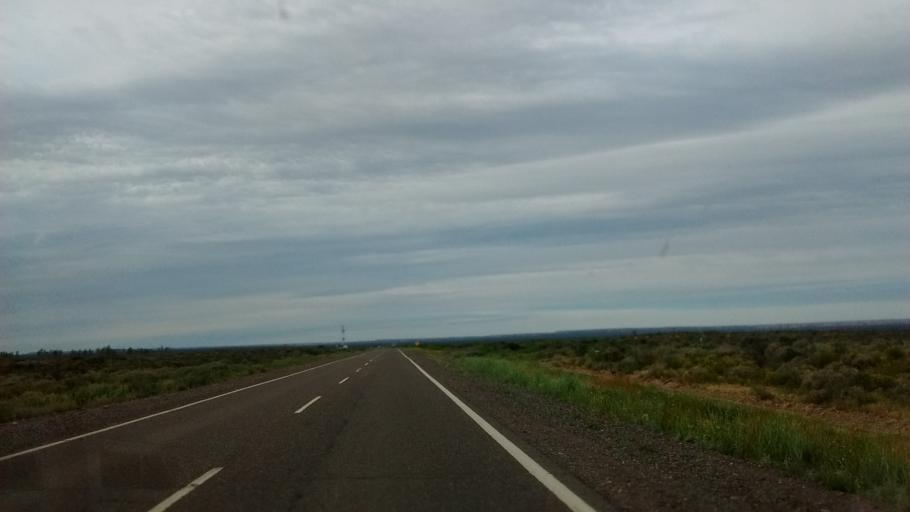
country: AR
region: Rio Negro
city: Catriel
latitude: -38.0168
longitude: -67.9141
